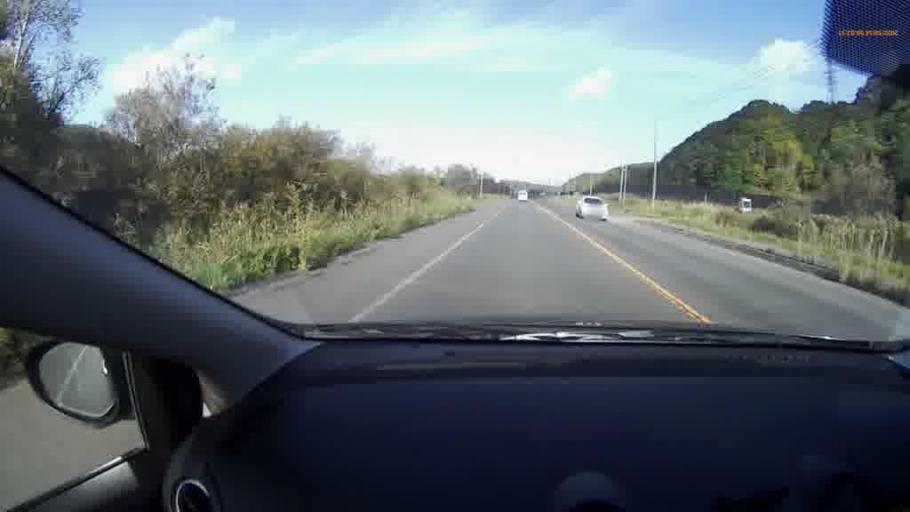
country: JP
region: Hokkaido
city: Kushiro
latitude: 42.9921
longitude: 144.4526
